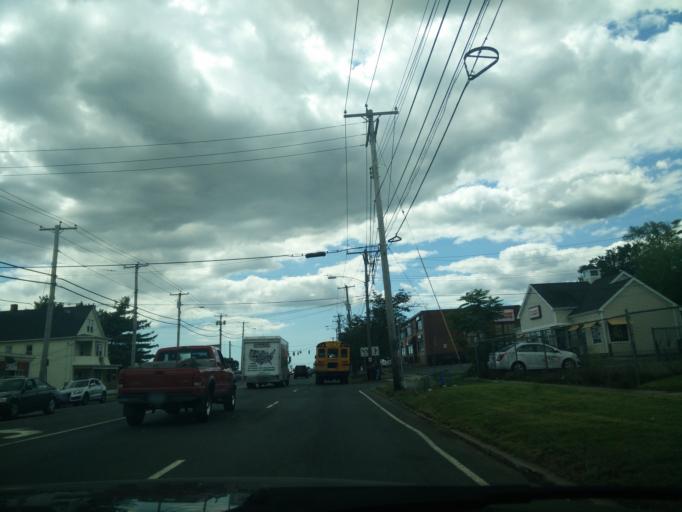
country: US
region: Connecticut
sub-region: New Haven County
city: Hamden
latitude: 41.3641
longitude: -72.9230
